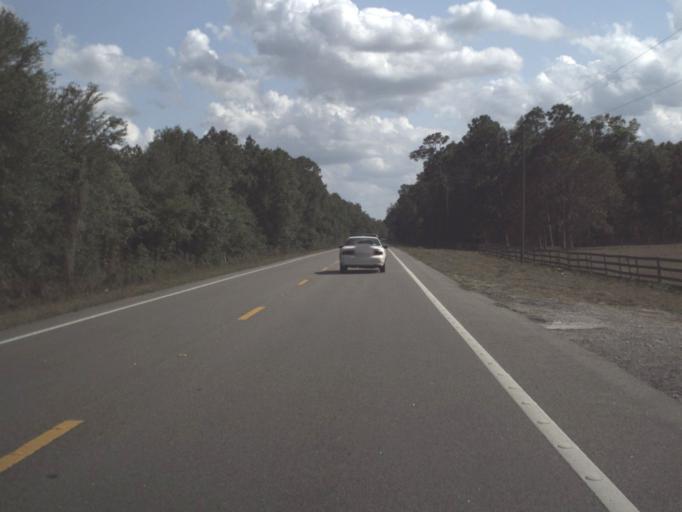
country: US
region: Florida
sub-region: Hernando County
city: Ridge Manor
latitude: 28.5433
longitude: -82.0909
